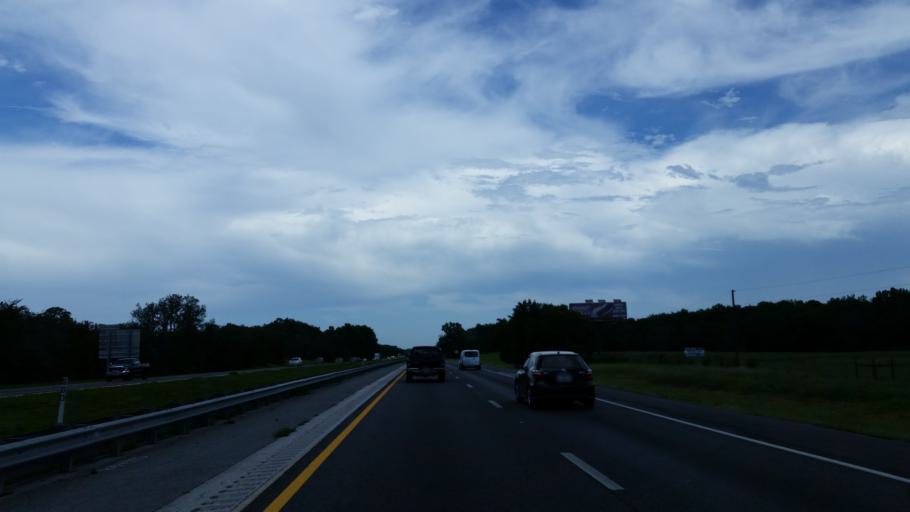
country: US
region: Florida
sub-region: Sumter County
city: Lake Panasoffkee
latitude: 28.7829
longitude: -82.0869
